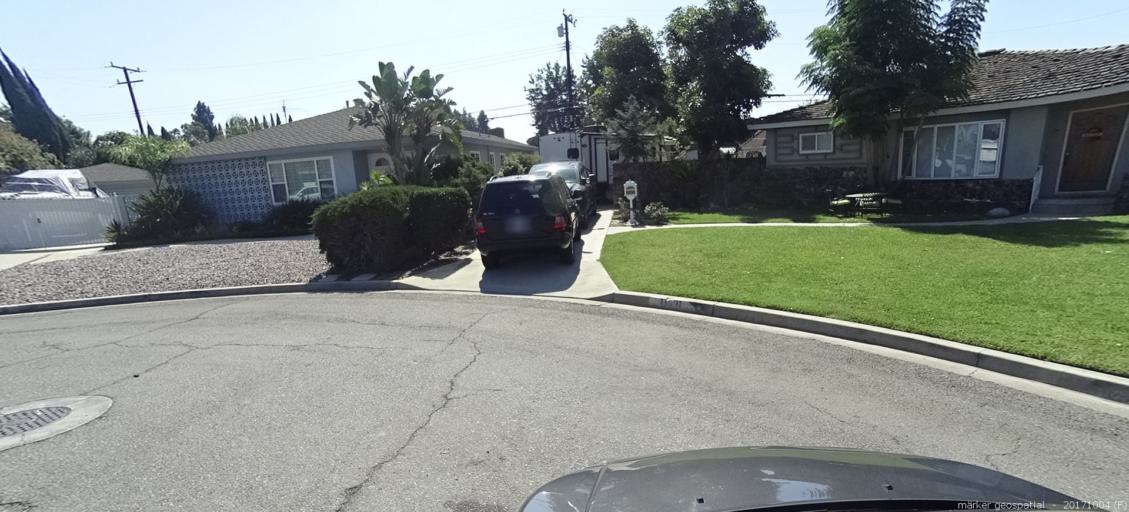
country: US
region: California
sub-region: Orange County
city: Garden Grove
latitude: 33.7949
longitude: -117.9553
